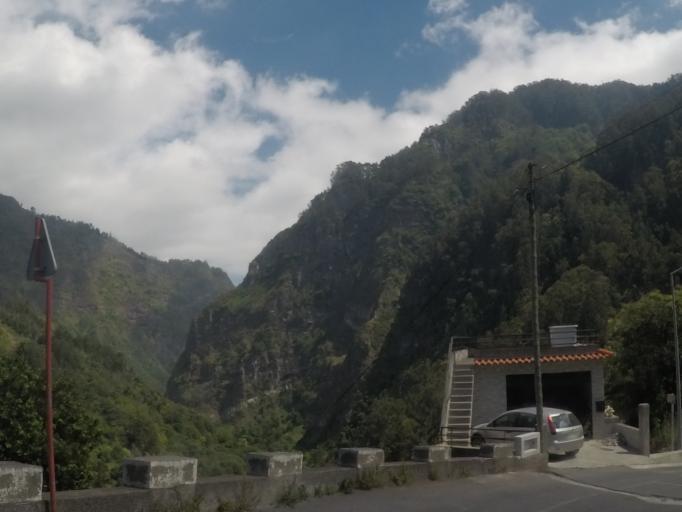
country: PT
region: Madeira
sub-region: Camara de Lobos
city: Curral das Freiras
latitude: 32.7080
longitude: -16.9734
